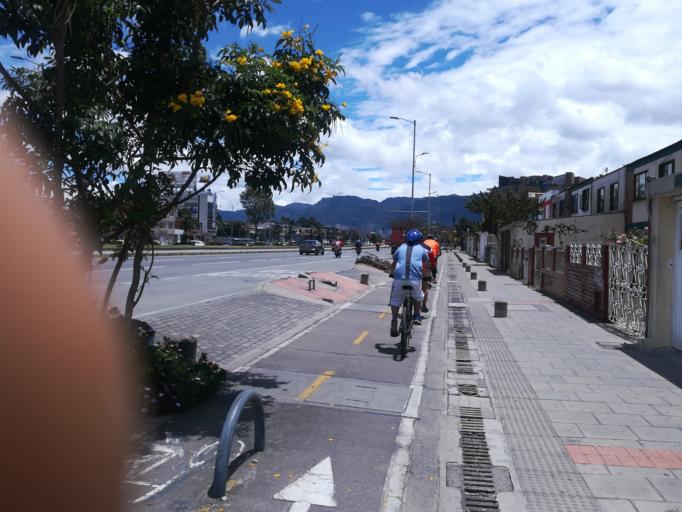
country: CO
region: Bogota D.C.
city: Bogota
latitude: 4.5952
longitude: -74.1154
